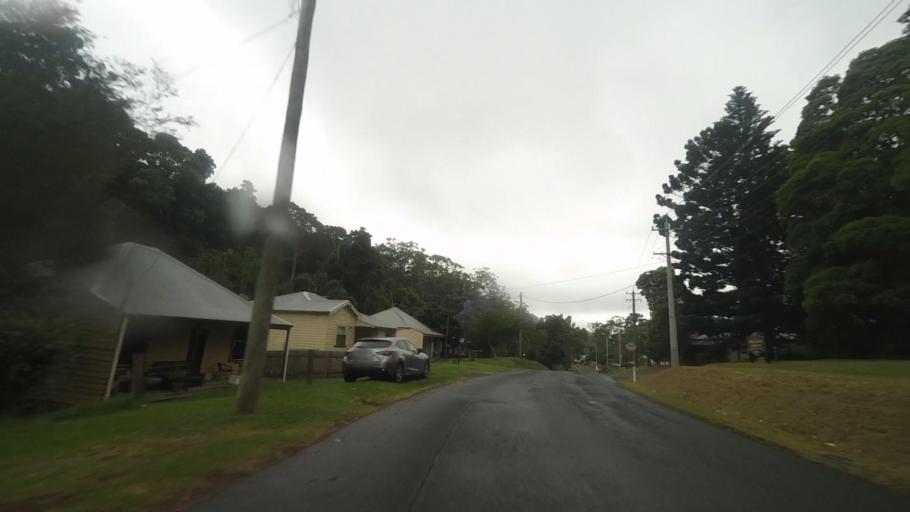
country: AU
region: New South Wales
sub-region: Wollongong
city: Cordeaux Heights
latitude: -34.4304
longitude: 150.8067
